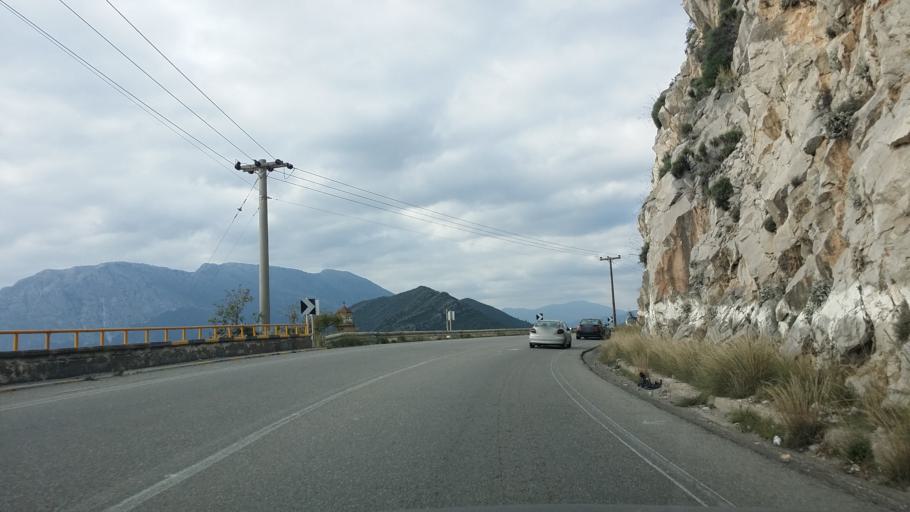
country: GR
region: West Greece
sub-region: Nomos Aitolias kai Akarnanias
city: Antirrio
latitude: 38.3498
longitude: 21.6727
